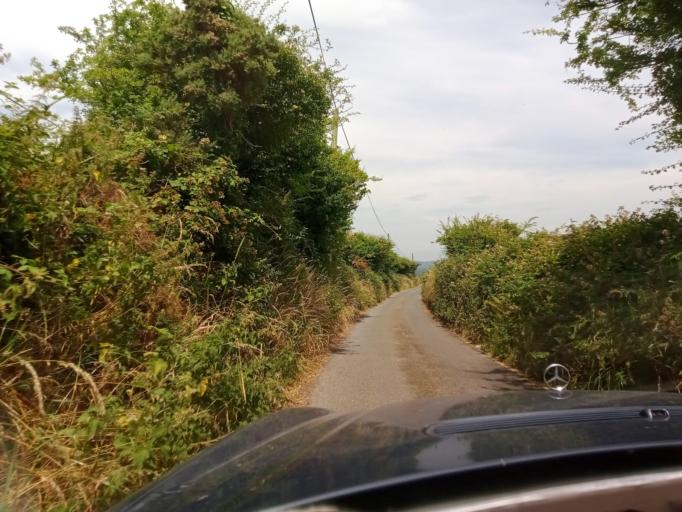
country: IE
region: Leinster
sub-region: Kilkenny
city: Mooncoin
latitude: 52.2645
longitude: -7.2155
